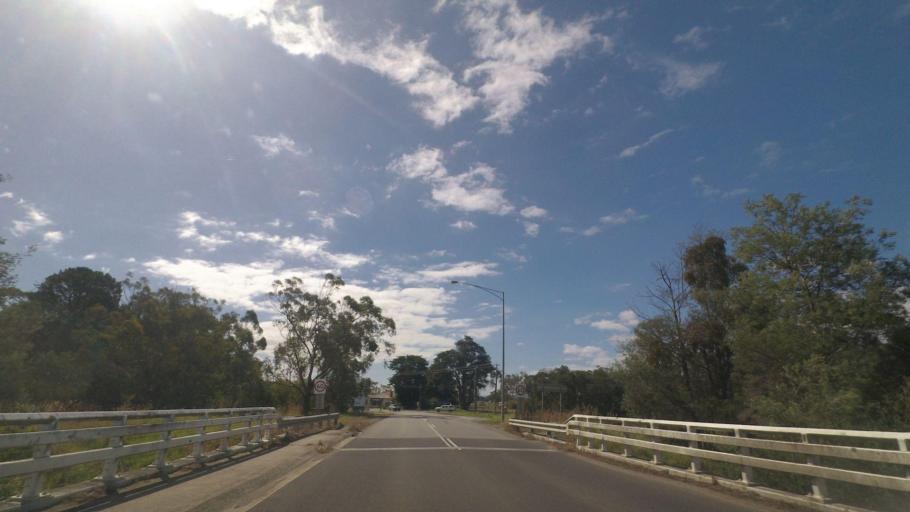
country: AU
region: Victoria
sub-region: Cardinia
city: Pakenham South
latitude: -38.1797
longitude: 145.5733
